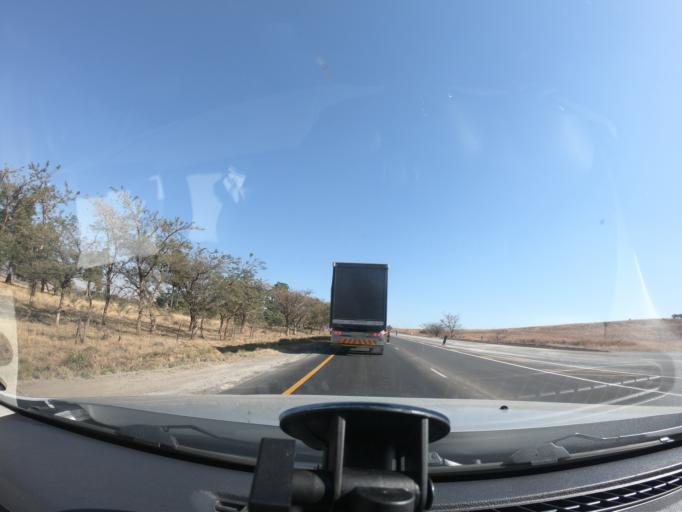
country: ZA
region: KwaZulu-Natal
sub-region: uThukela District Municipality
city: Bergville
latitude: -28.4344
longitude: 29.4740
